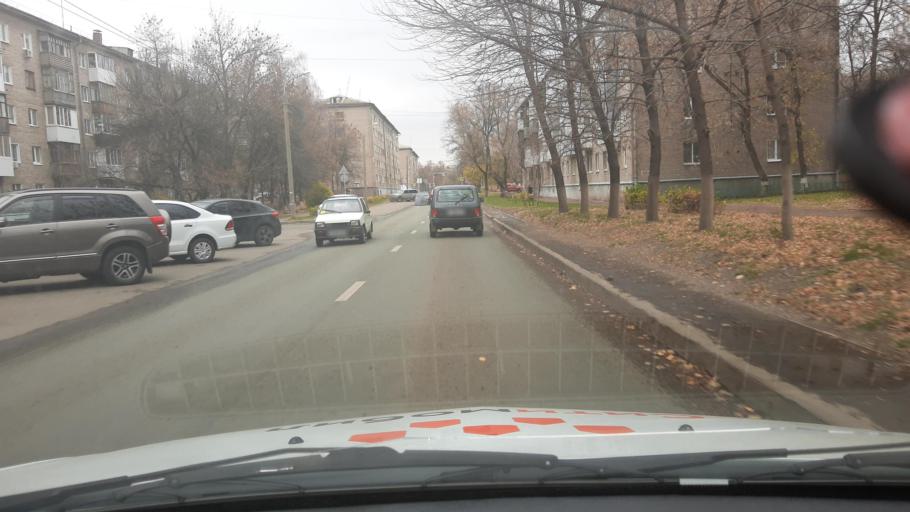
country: RU
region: Bashkortostan
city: Ufa
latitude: 54.7887
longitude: 56.0301
